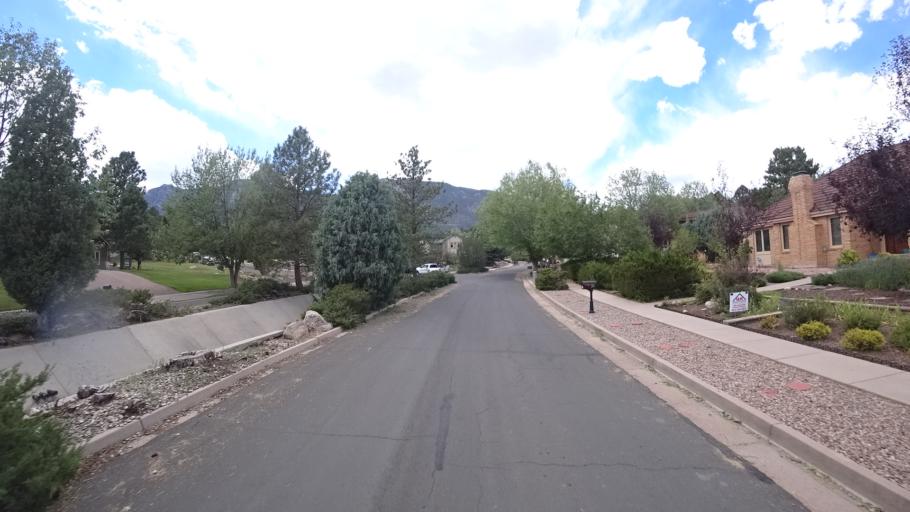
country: US
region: Colorado
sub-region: El Paso County
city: Stratmoor
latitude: 38.7729
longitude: -104.8280
